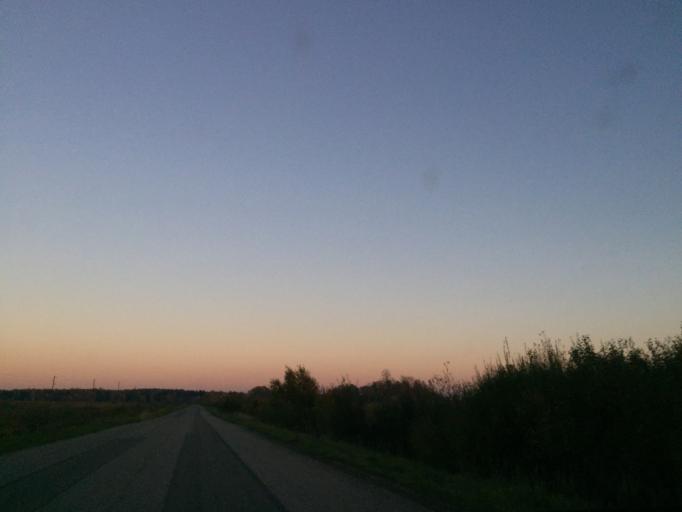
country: LT
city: Vieksniai
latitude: 56.4014
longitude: 22.5368
